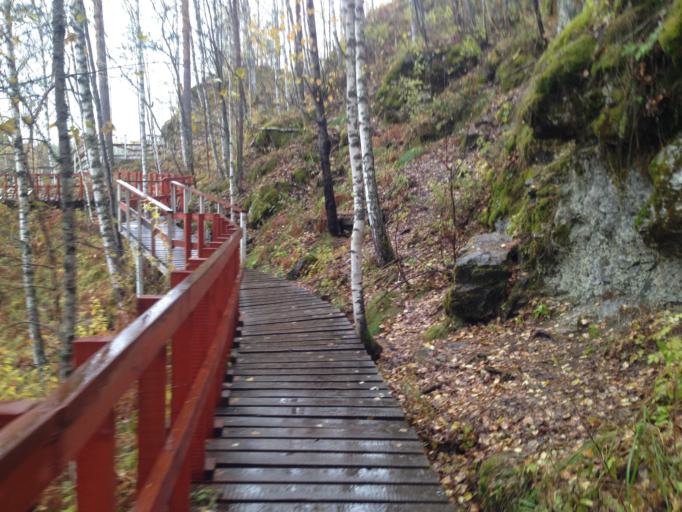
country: RU
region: Sverdlovsk
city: Nizhniye Sergi
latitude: 56.5181
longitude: 59.2555
